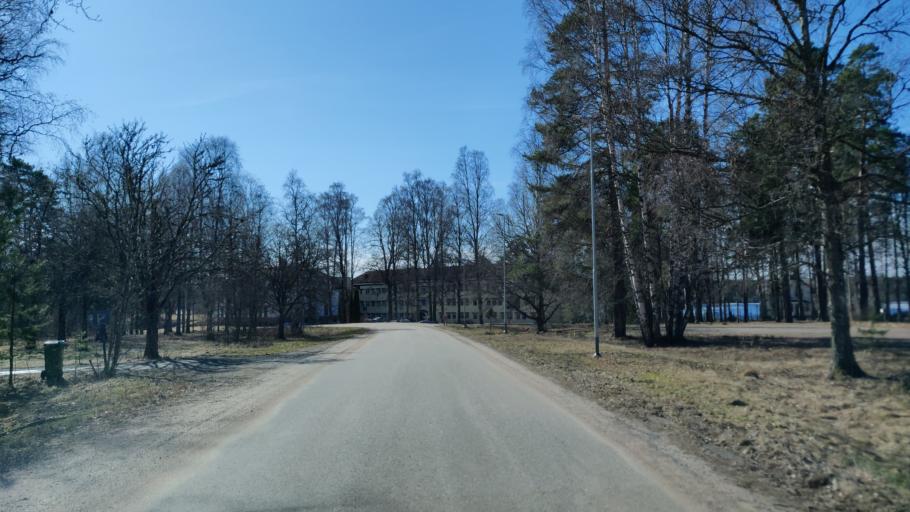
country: SE
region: Vaermland
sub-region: Hagfors Kommun
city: Hagfors
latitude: 60.0208
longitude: 13.6200
